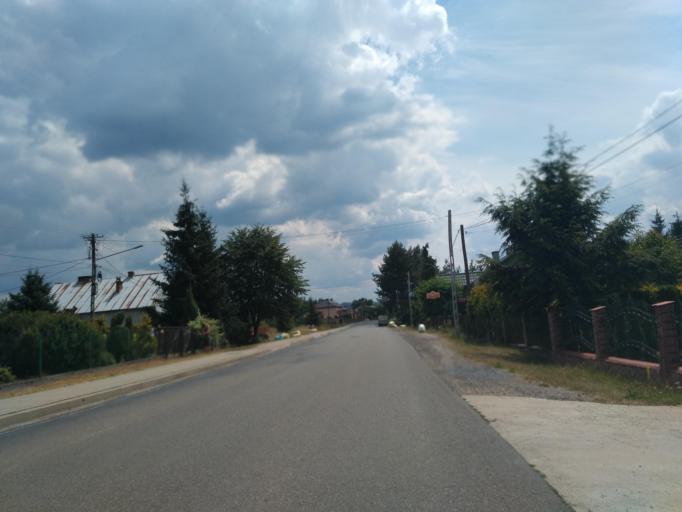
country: PL
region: Subcarpathian Voivodeship
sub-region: Powiat debicki
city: Pilzno
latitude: 50.0299
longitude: 21.2942
